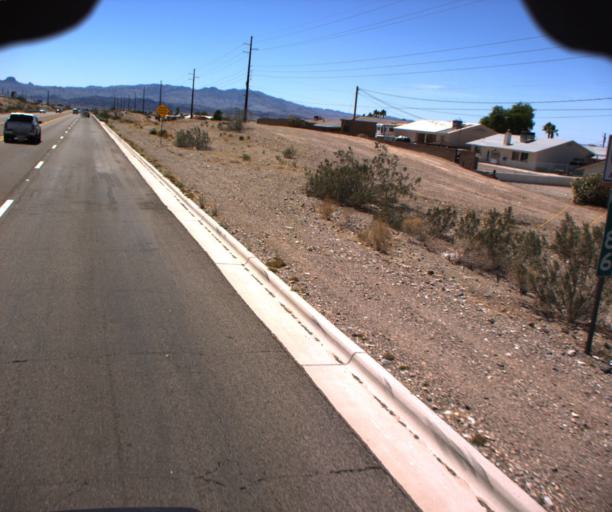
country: US
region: Arizona
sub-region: Mohave County
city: Desert Hills
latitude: 34.5249
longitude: -114.3496
